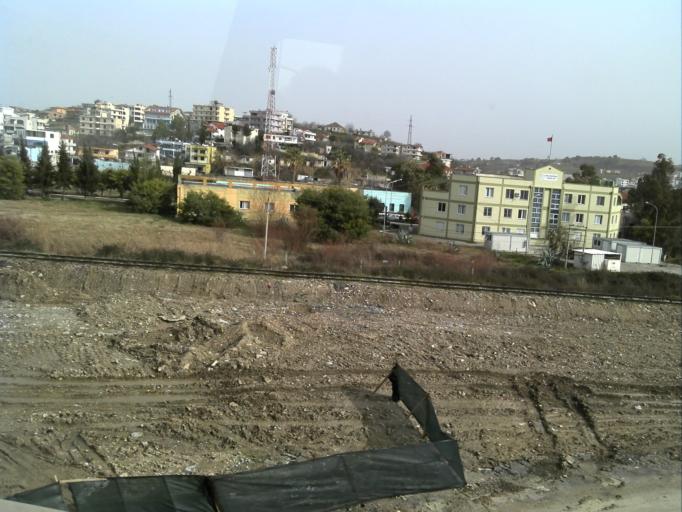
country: AL
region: Durres
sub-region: Rrethi i Durresit
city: Rrashbull
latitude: 41.2915
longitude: 19.5103
